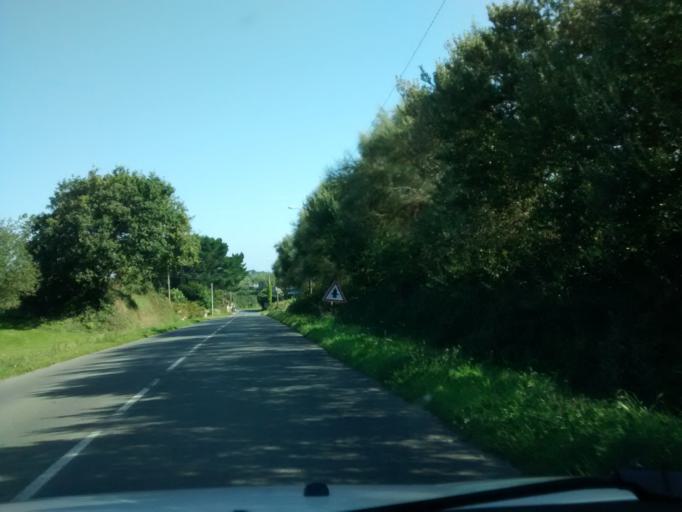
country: FR
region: Brittany
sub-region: Departement des Cotes-d'Armor
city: Pleubian
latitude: 48.8493
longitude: -3.1300
